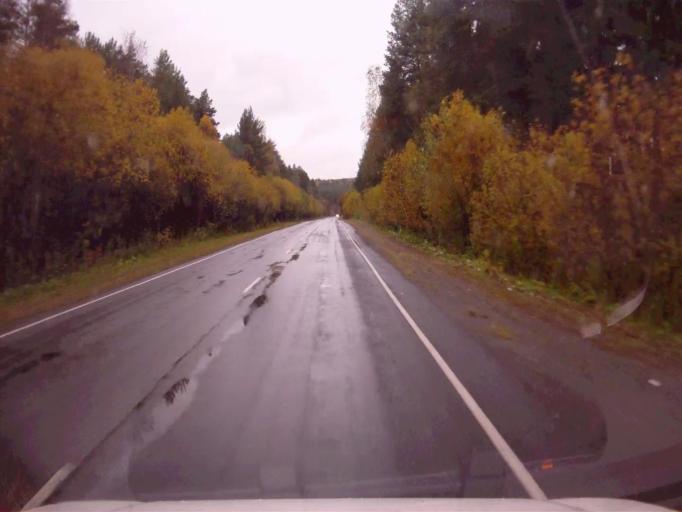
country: RU
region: Chelyabinsk
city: Verkhniy Ufaley
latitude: 56.0492
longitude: 60.1449
